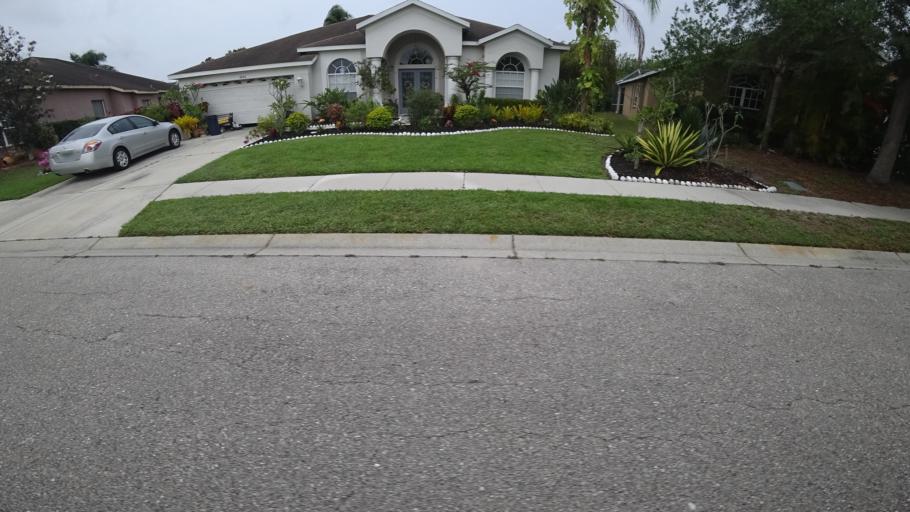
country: US
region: Florida
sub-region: Manatee County
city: Samoset
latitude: 27.4569
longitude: -82.5007
